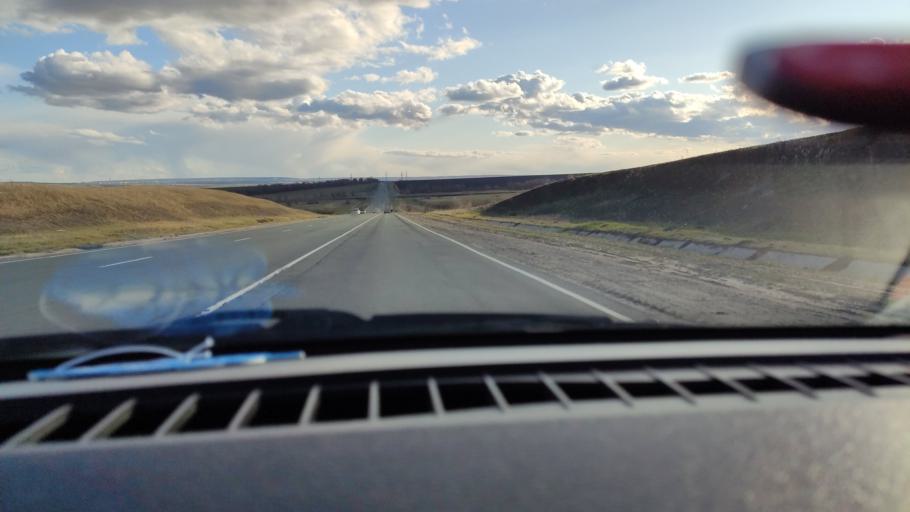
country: RU
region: Saratov
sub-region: Saratovskiy Rayon
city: Saratov
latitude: 51.7546
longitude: 46.0643
